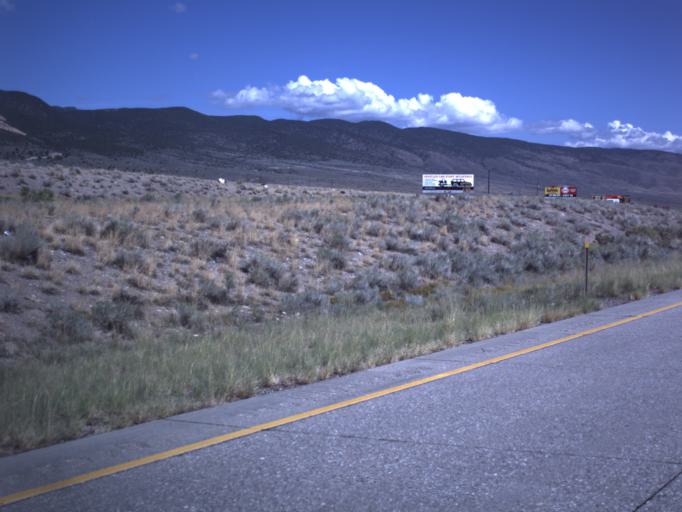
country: US
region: Utah
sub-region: Sevier County
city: Monroe
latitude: 38.6070
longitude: -112.2334
